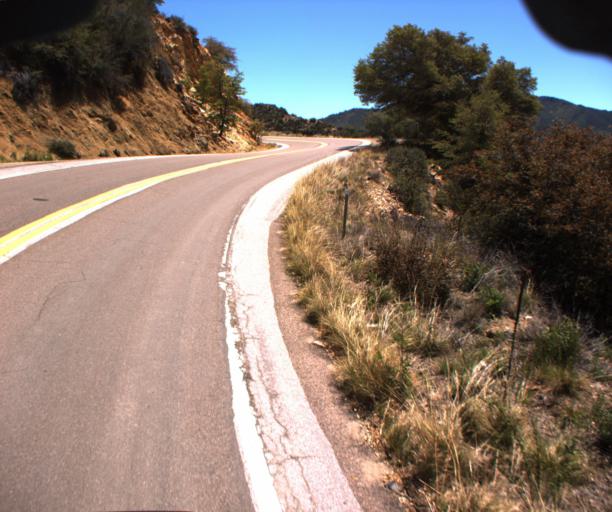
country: US
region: Arizona
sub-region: Yavapai County
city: Prescott
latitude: 34.4538
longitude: -112.5257
